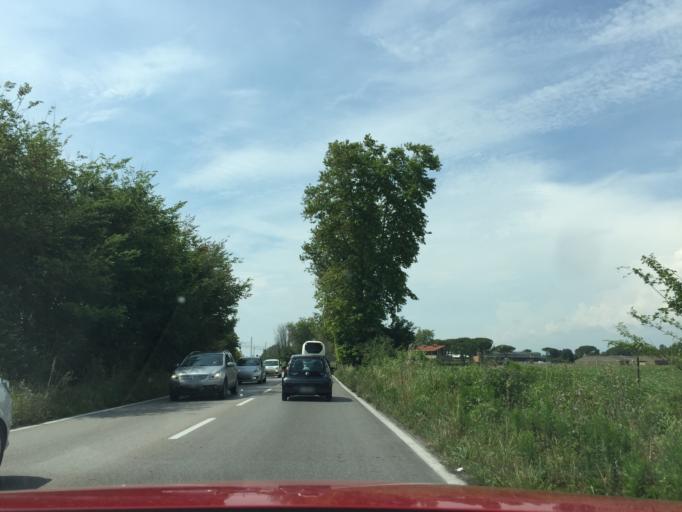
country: IT
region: Tuscany
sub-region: Province of Pisa
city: Migliarino
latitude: 43.7539
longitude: 10.3557
